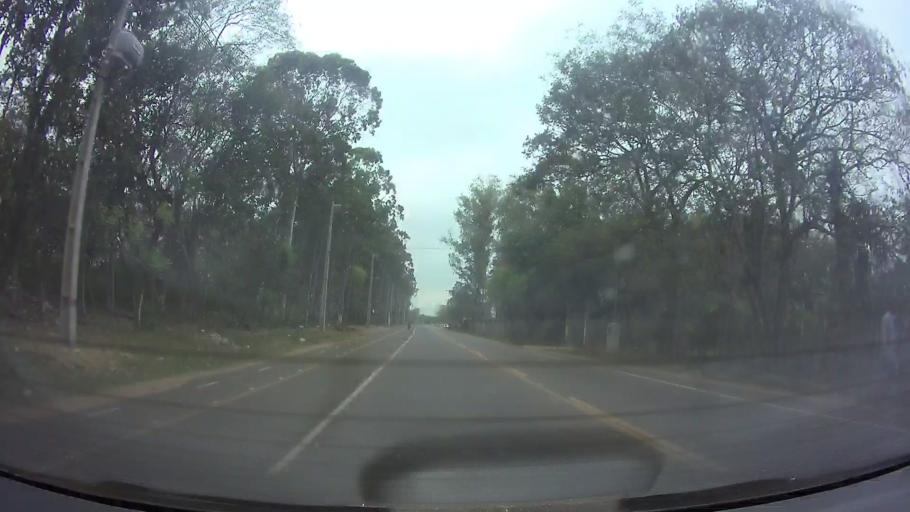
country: PY
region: Central
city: Limpio
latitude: -25.2189
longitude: -57.4175
